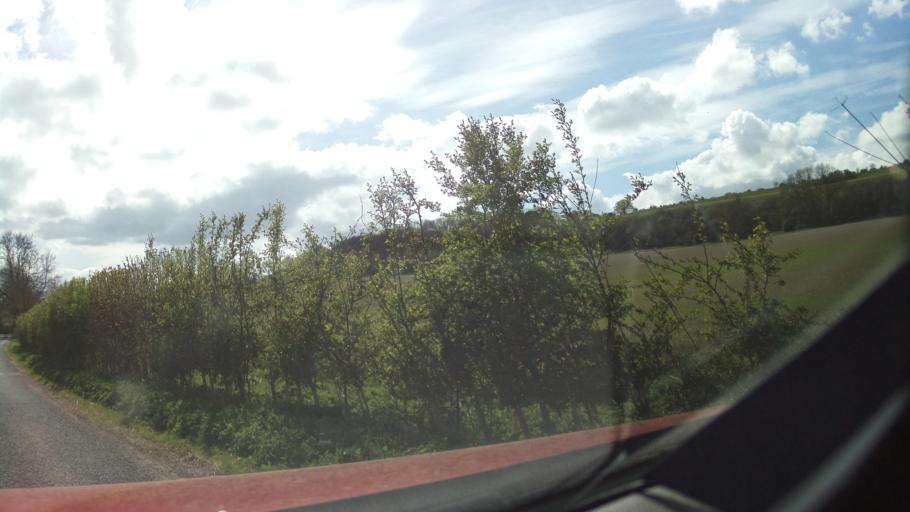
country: GB
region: England
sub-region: West Berkshire
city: Kintbury
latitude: 51.3366
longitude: -1.4698
